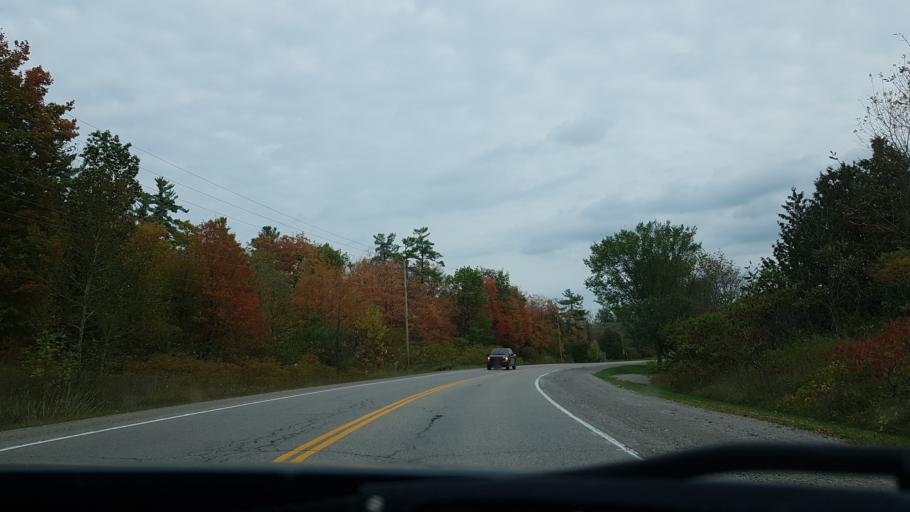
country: CA
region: Ontario
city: Omemee
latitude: 44.5320
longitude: -78.7560
